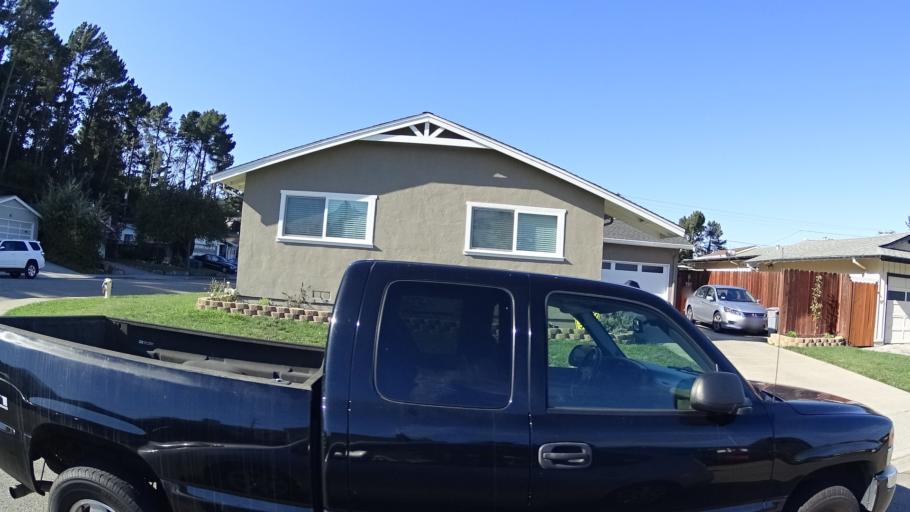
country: US
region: California
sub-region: San Mateo County
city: San Bruno
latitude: 37.6326
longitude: -122.4420
